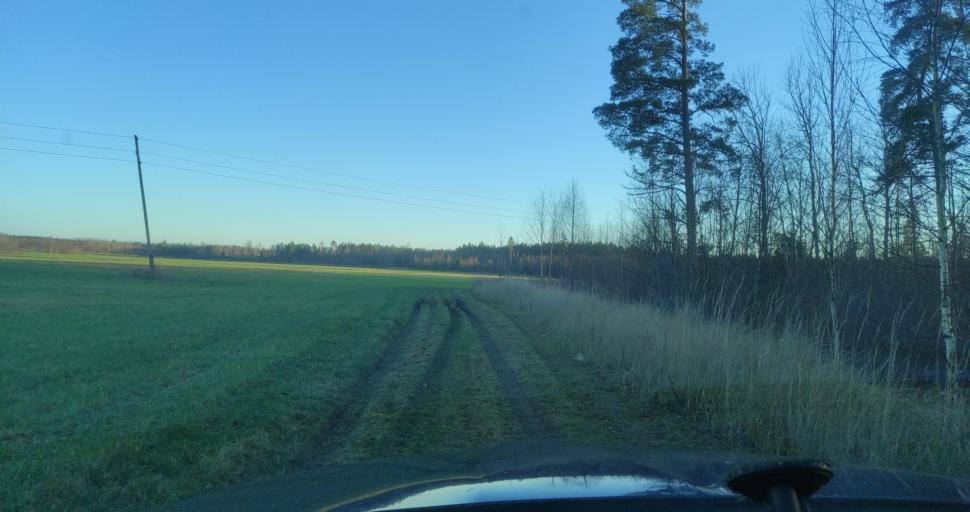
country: LV
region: Dundaga
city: Dundaga
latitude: 57.3833
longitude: 22.0857
